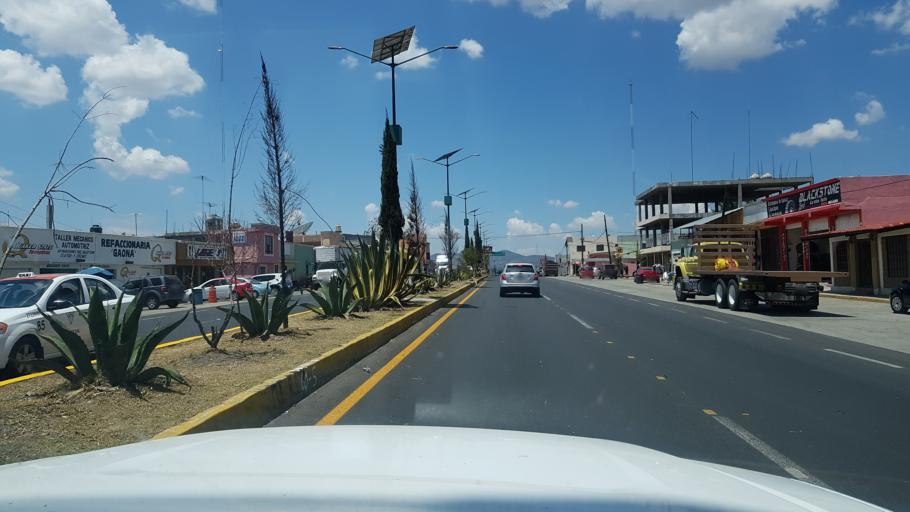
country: MX
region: Hidalgo
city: Calpulalpan
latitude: 19.5920
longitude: -98.5646
